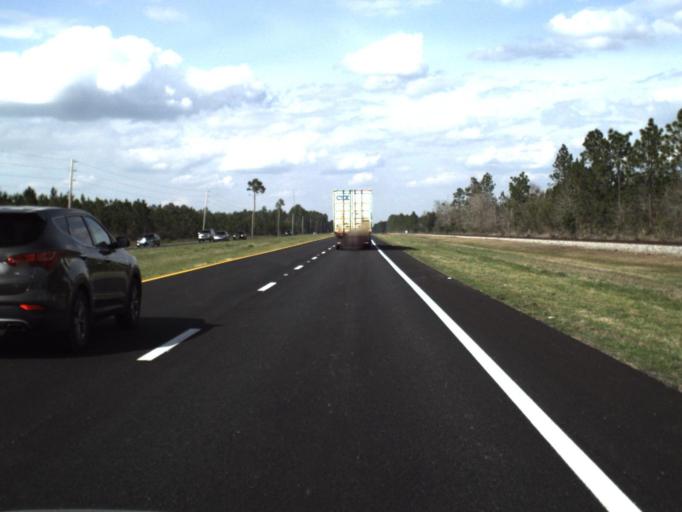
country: US
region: Florida
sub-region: Bay County
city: Youngstown
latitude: 30.4133
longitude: -85.4306
